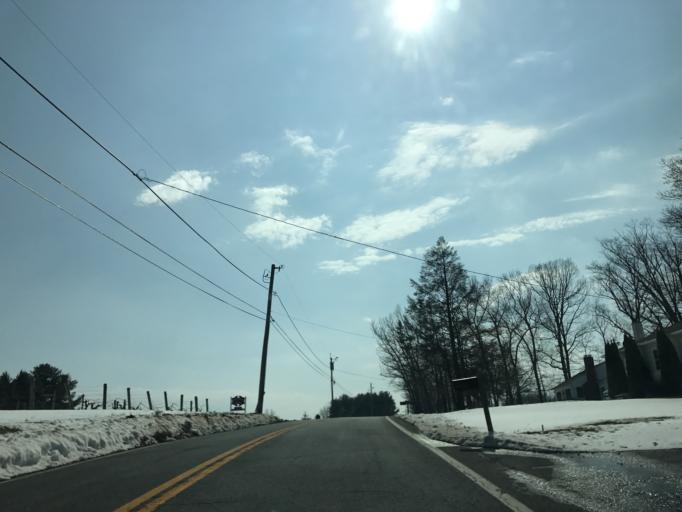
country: US
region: Pennsylvania
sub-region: York County
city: Susquehanna Trails
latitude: 39.7108
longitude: -76.4018
